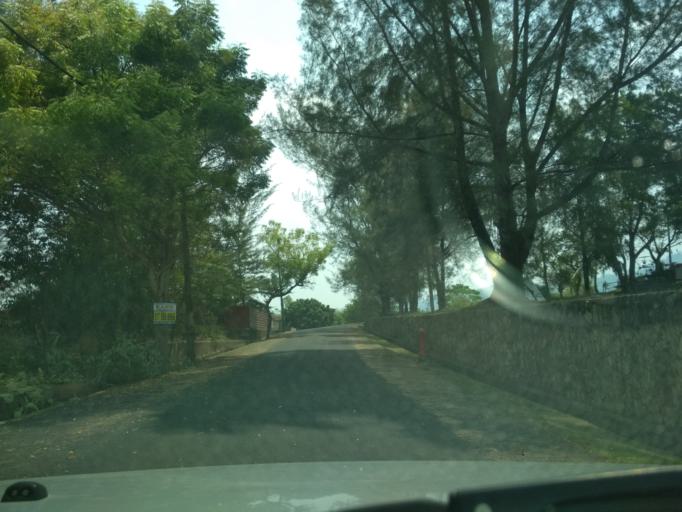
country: MY
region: Kedah
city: Kulim
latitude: 5.3562
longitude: 100.5281
